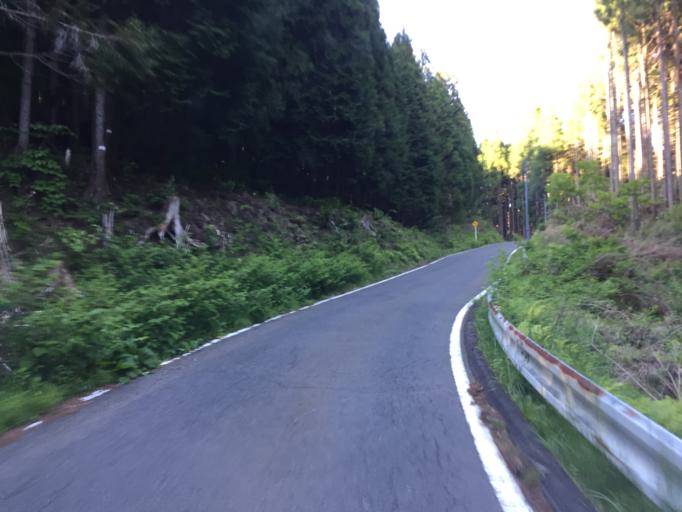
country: JP
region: Ibaraki
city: Kitaibaraki
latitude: 36.9012
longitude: 140.5934
